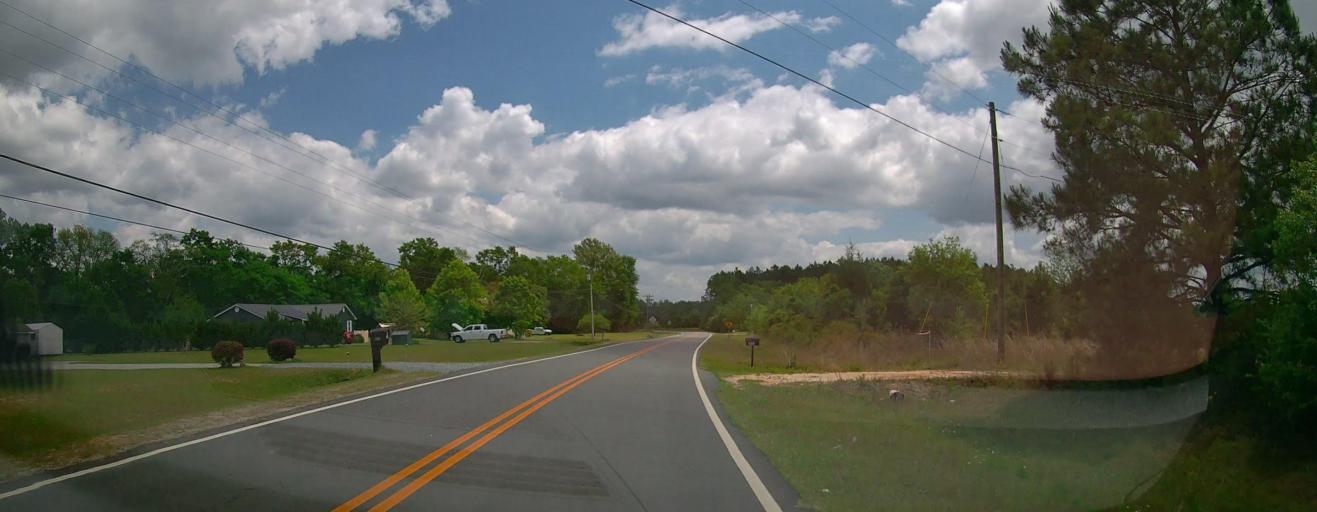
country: US
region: Georgia
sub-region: Laurens County
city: Dublin
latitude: 32.6004
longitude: -82.9603
